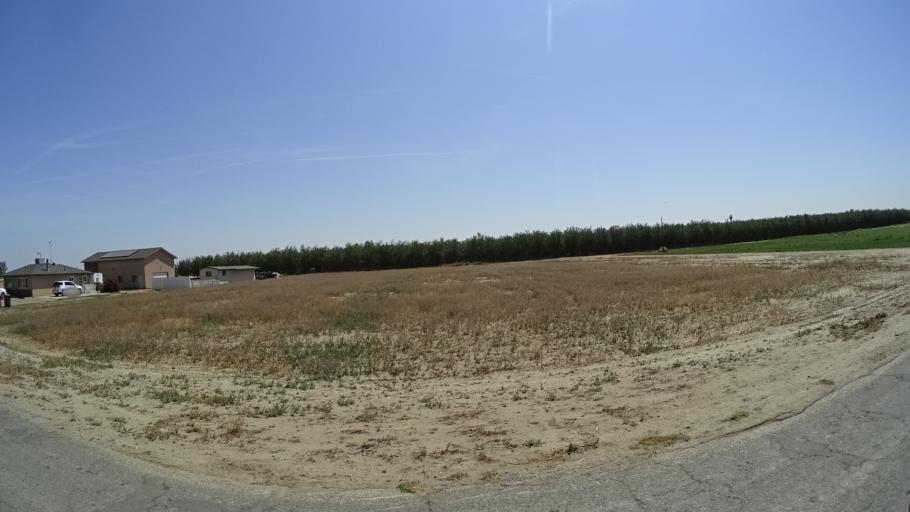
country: US
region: California
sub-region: Fresno County
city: Riverdale
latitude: 36.3976
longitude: -119.8693
